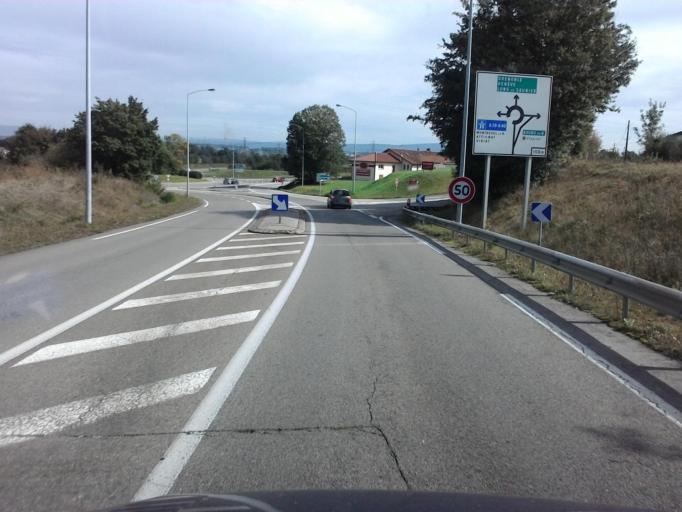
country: FR
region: Rhone-Alpes
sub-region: Departement de l'Ain
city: Viriat
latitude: 46.2327
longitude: 5.1980
